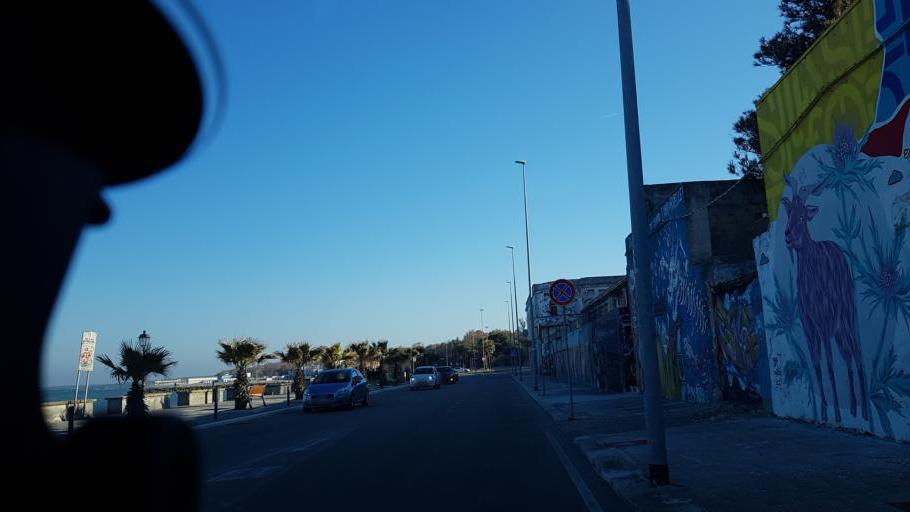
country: IT
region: Apulia
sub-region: Provincia di Lecce
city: Struda
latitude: 40.3854
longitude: 18.3045
